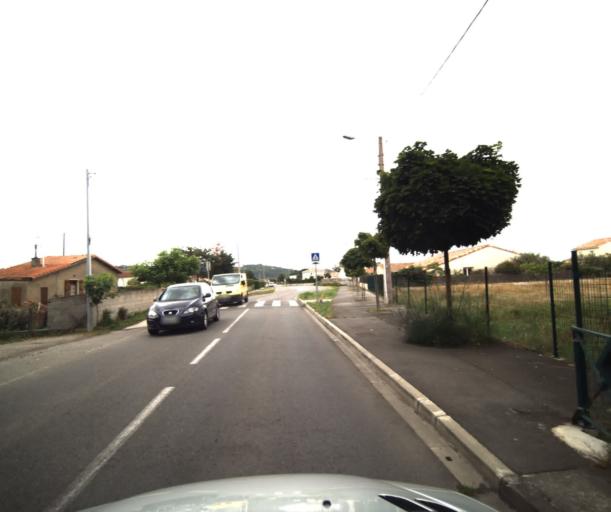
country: FR
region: Midi-Pyrenees
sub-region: Departement de la Haute-Garonne
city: Pinsaguel
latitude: 43.4978
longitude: 1.3950
